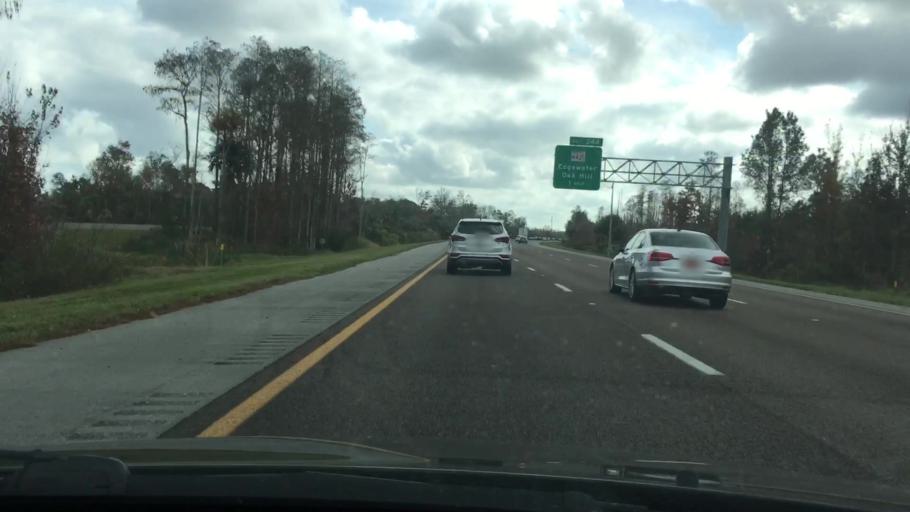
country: US
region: Florida
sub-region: Volusia County
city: Glencoe
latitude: 28.9700
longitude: -80.9602
